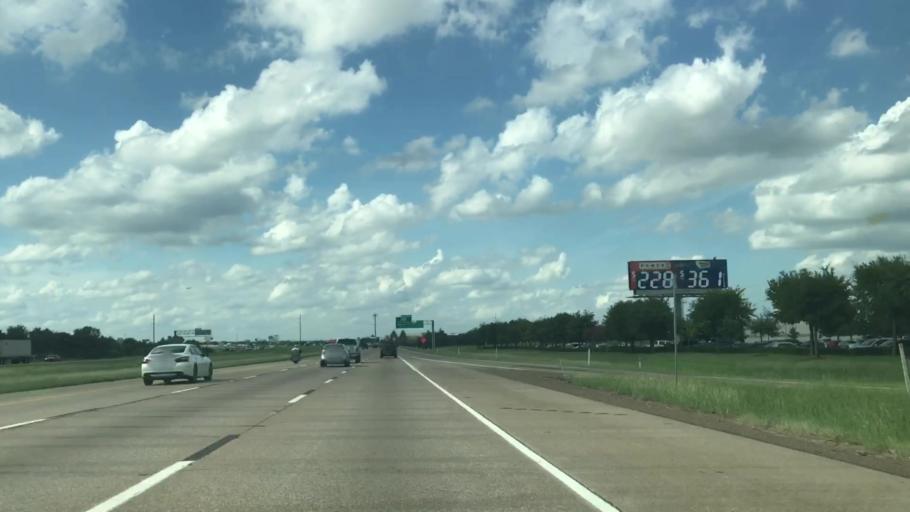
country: US
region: Texas
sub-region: Dallas County
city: Coppell
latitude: 32.9375
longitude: -97.0100
